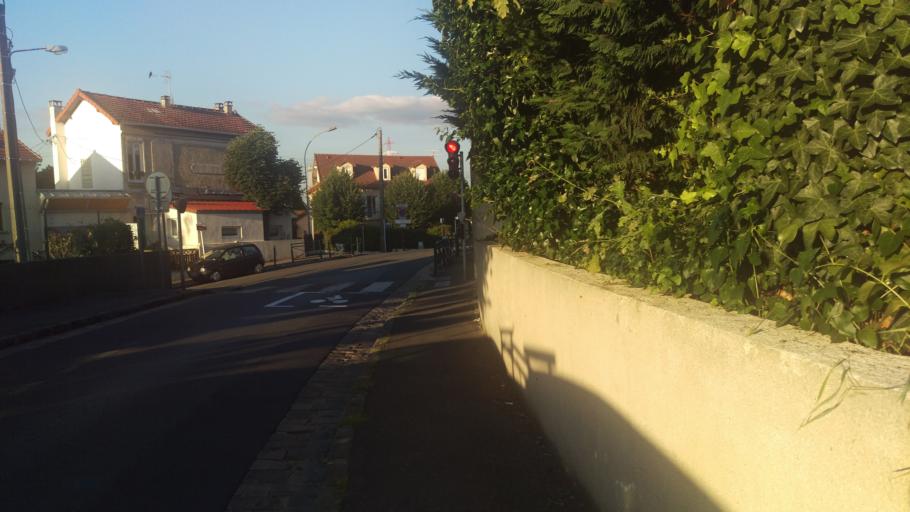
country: FR
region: Ile-de-France
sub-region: Departement de l'Essonne
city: Palaiseau
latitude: 48.7276
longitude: 2.2345
